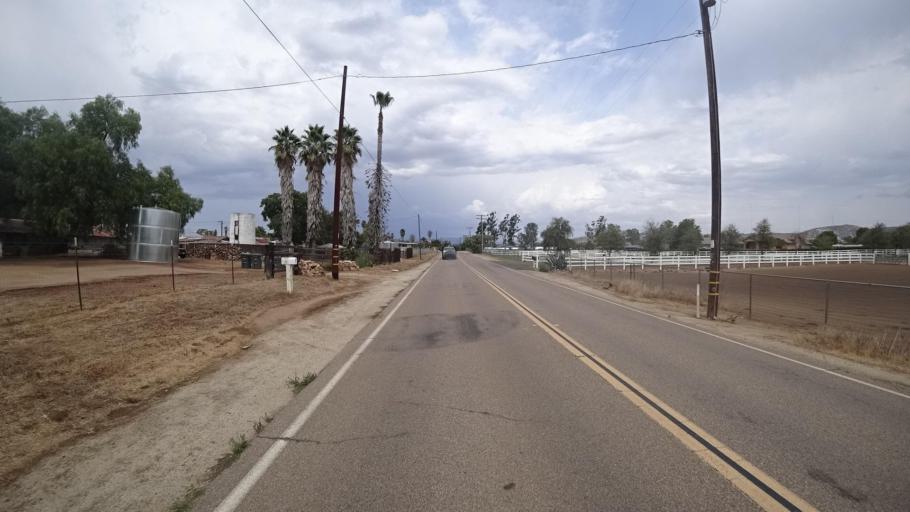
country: US
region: California
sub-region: San Diego County
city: Ramona
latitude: 33.0601
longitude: -116.8607
